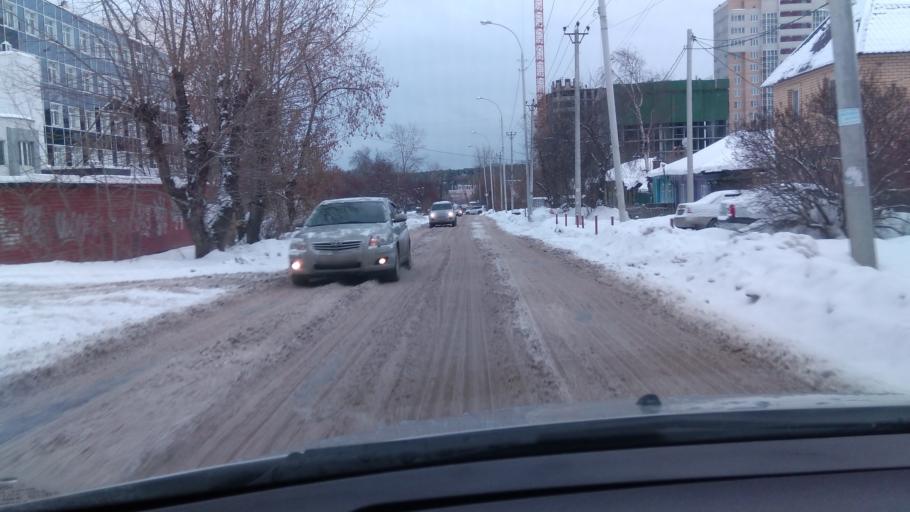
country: RU
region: Sverdlovsk
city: Yekaterinburg
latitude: 56.8029
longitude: 60.5973
